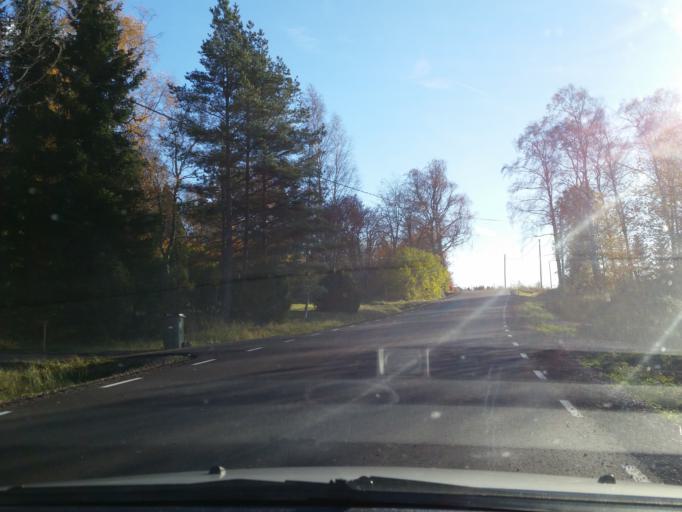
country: AX
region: Alands landsbygd
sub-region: Jomala
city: Jomala
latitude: 60.1906
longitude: 19.9606
